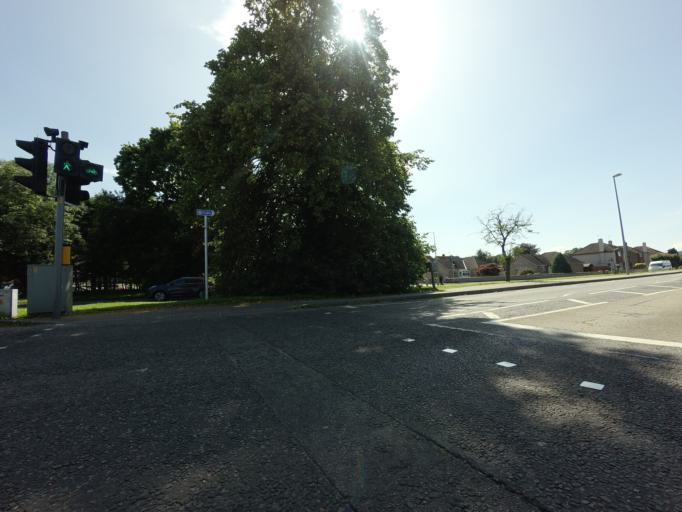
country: GB
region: Scotland
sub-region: Highland
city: Inverness
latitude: 57.4721
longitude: -4.1920
